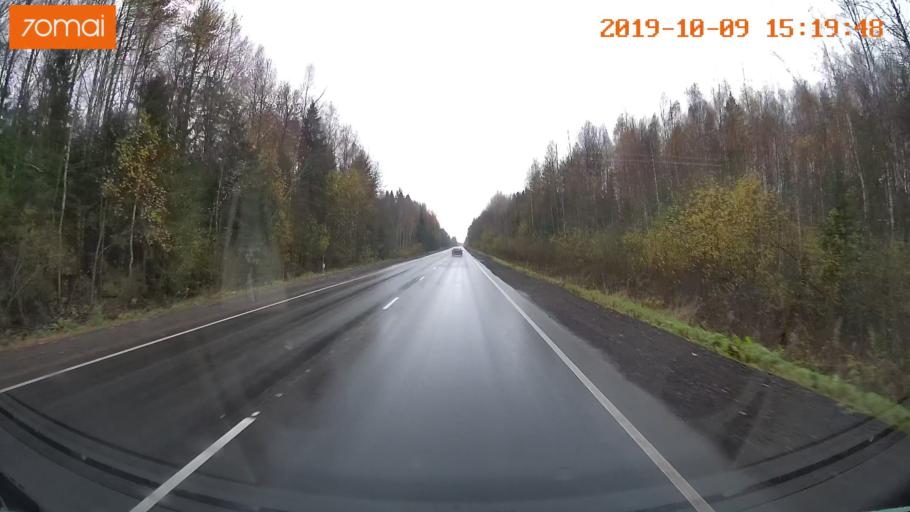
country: RU
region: Kostroma
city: Susanino
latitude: 58.0716
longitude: 41.5497
